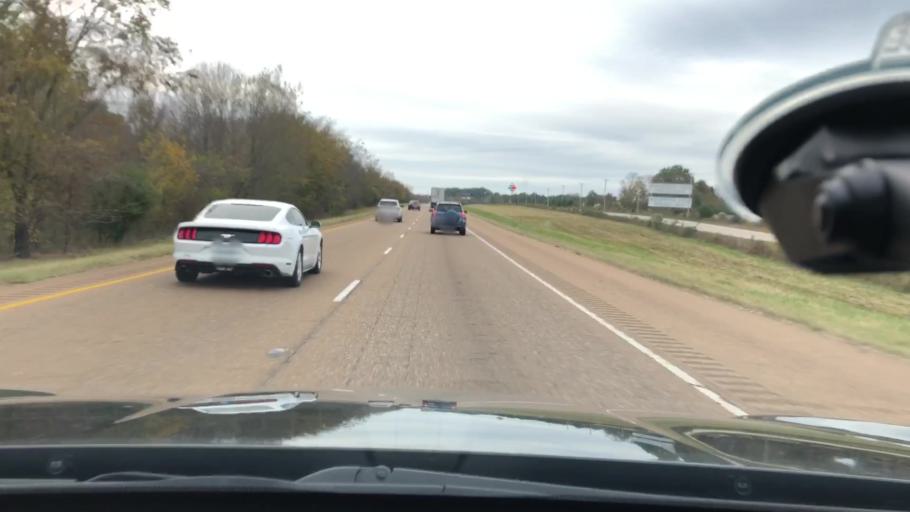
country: US
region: Arkansas
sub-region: Nevada County
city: Prescott
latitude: 33.8220
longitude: -93.4074
